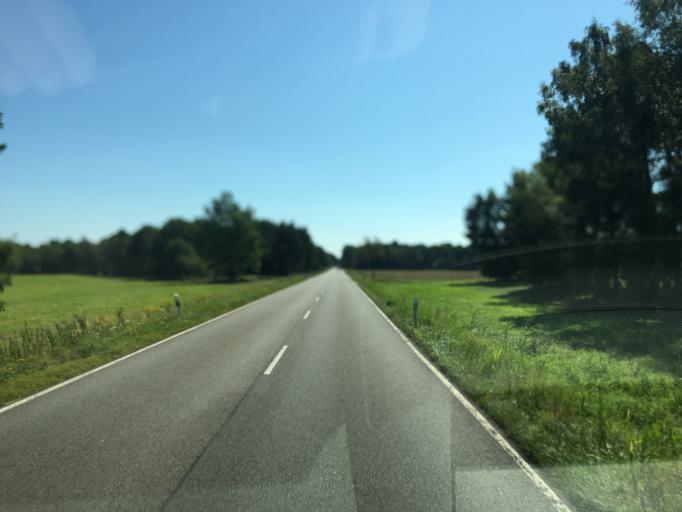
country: DE
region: Brandenburg
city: Welzow
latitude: 51.5717
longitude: 14.0976
